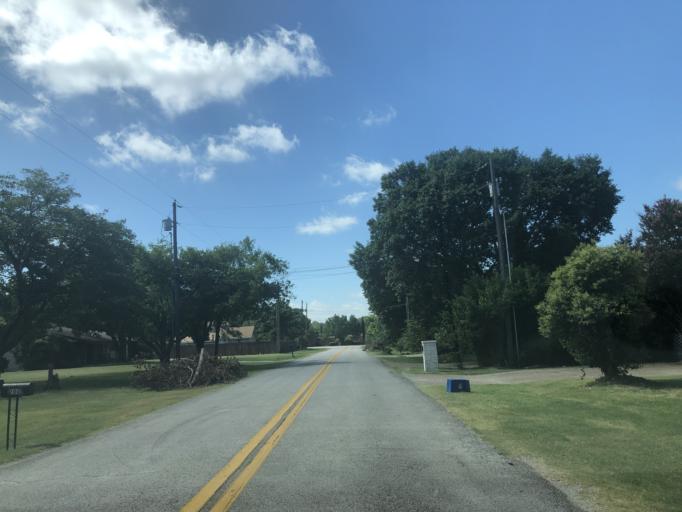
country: US
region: Texas
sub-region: Dallas County
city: Duncanville
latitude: 32.6495
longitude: -96.9355
